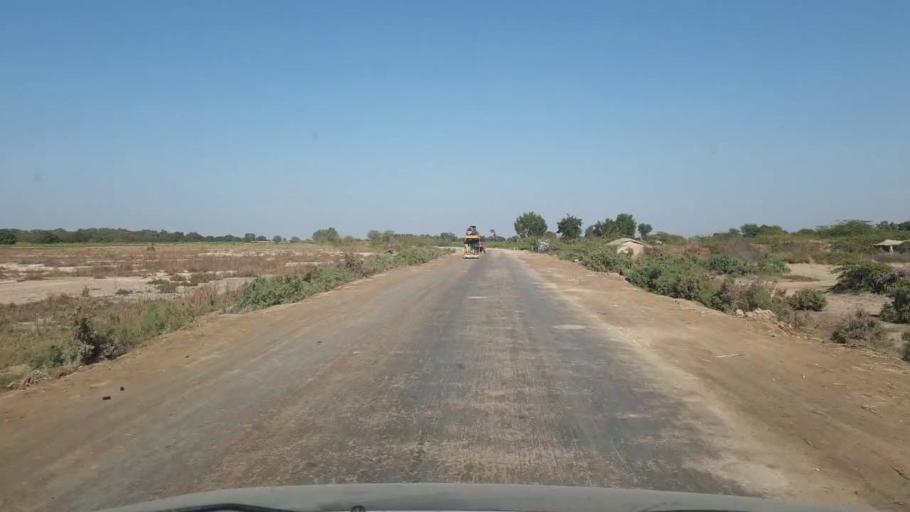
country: PK
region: Sindh
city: Samaro
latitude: 25.3312
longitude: 69.3065
